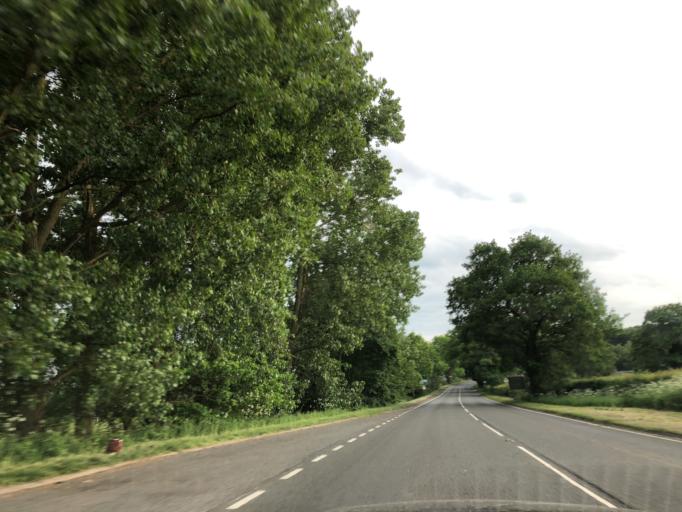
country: GB
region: England
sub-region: Warwickshire
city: Wroxall
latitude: 52.3317
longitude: -1.6623
